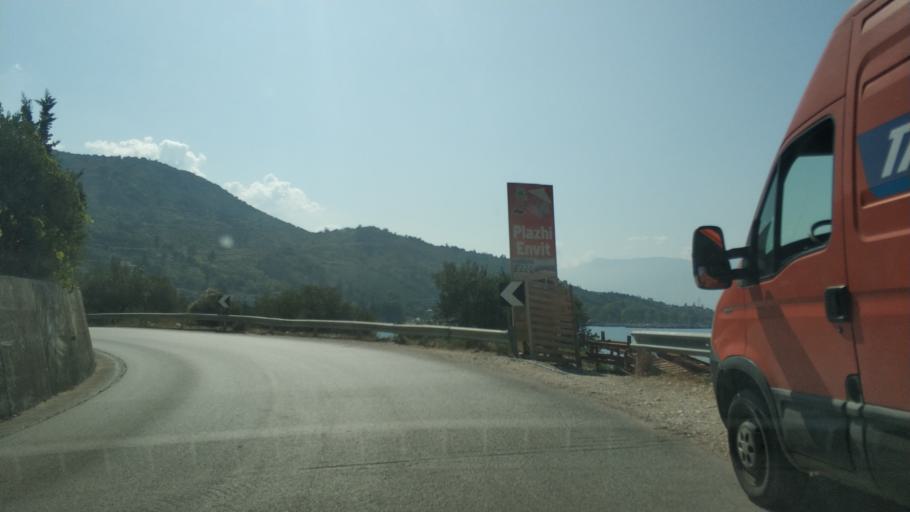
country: AL
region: Vlore
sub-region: Rrethi i Vlores
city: Orikum
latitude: 40.3885
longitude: 19.4819
